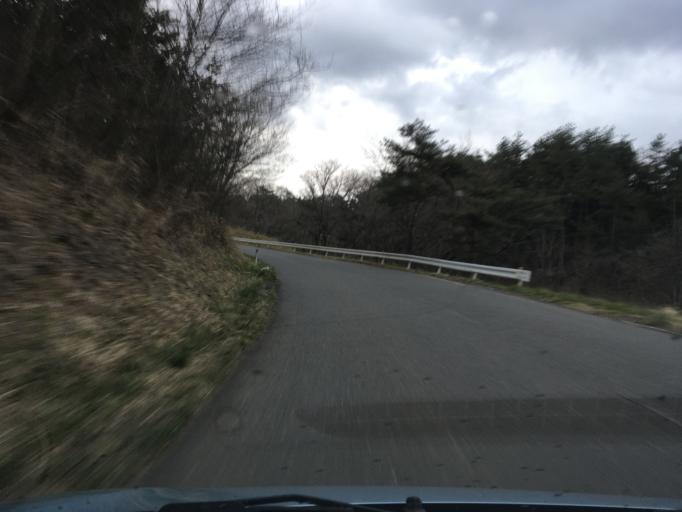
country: JP
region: Iwate
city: Ichinoseki
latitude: 38.7810
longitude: 141.2430
